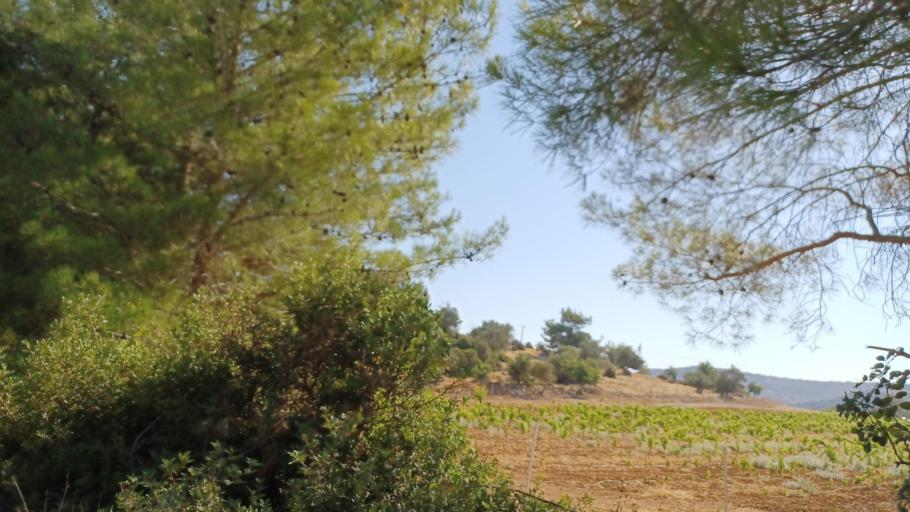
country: CY
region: Limassol
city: Pissouri
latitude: 34.7272
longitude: 32.6798
